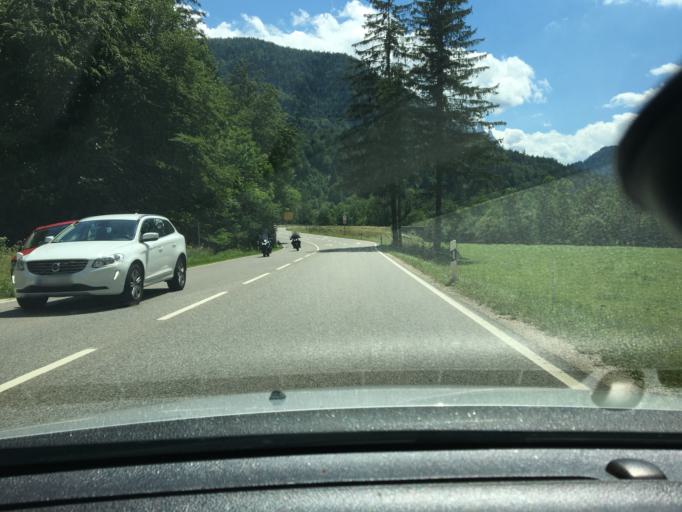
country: DE
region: Bavaria
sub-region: Upper Bavaria
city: Schneizlreuth
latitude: 47.6919
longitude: 12.8020
